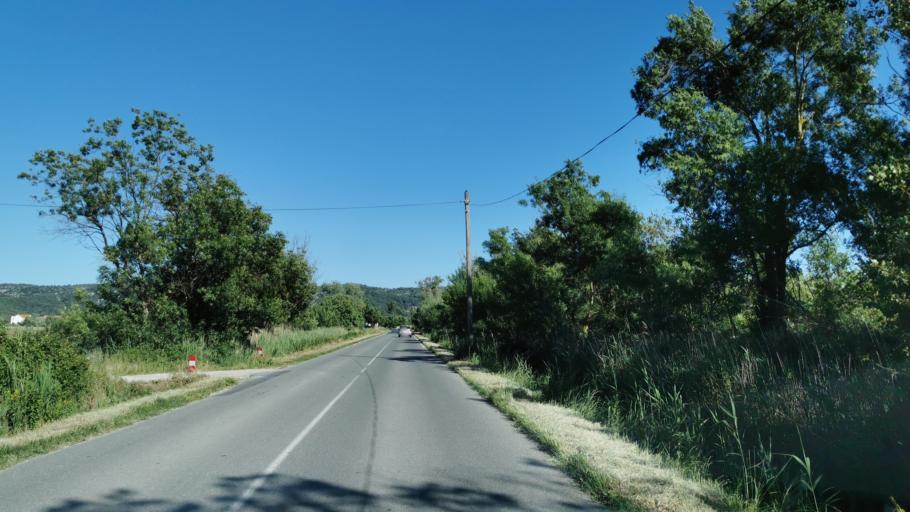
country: FR
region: Languedoc-Roussillon
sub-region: Departement de l'Aude
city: Narbonne
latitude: 43.1672
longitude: 3.0416
